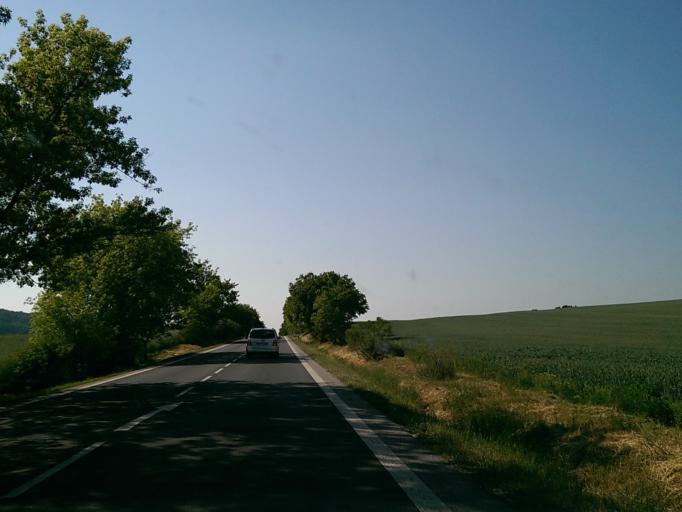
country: CZ
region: Liberecky
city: Rovensko pod Troskami
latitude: 50.5119
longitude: 15.2584
